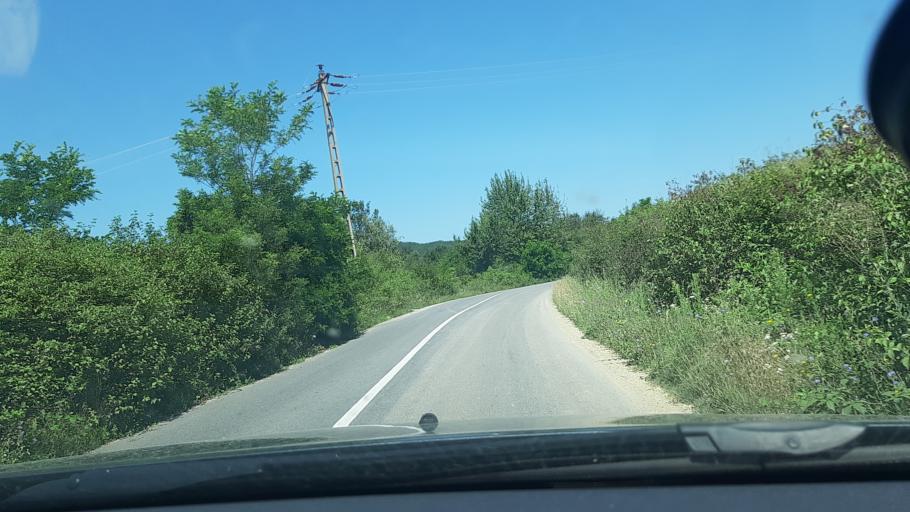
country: RO
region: Hunedoara
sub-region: Comuna Teliucu Inferior
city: Teliucu Inferior
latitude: 45.6948
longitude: 22.8757
